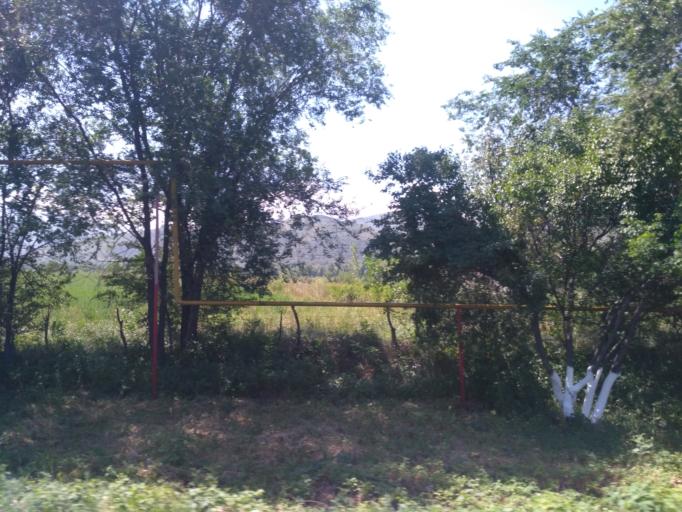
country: KZ
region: Almaty Oblysy
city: Burunday
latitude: 43.1665
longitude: 76.5943
